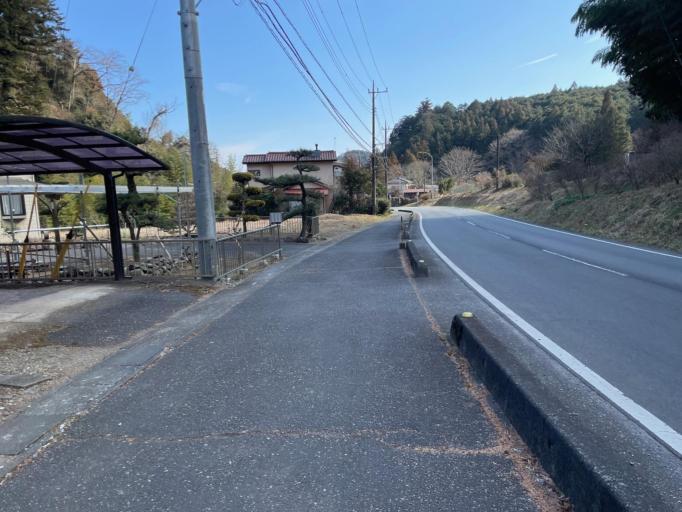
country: JP
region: Saitama
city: Hanno
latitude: 35.8456
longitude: 139.2605
